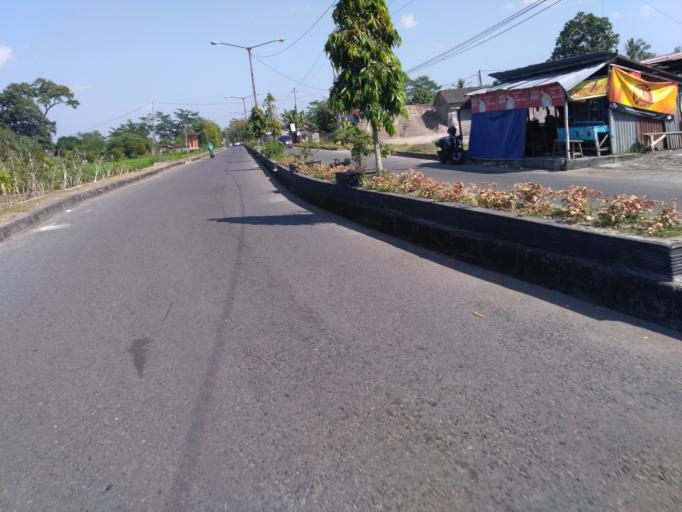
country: ID
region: Daerah Istimewa Yogyakarta
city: Depok
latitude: -7.7513
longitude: 110.4324
